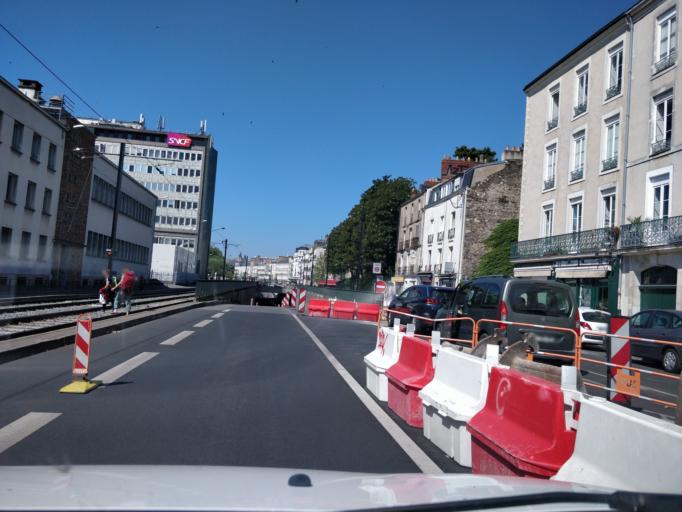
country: FR
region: Pays de la Loire
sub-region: Departement de la Loire-Atlantique
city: Nantes
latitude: 47.2184
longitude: -1.5399
